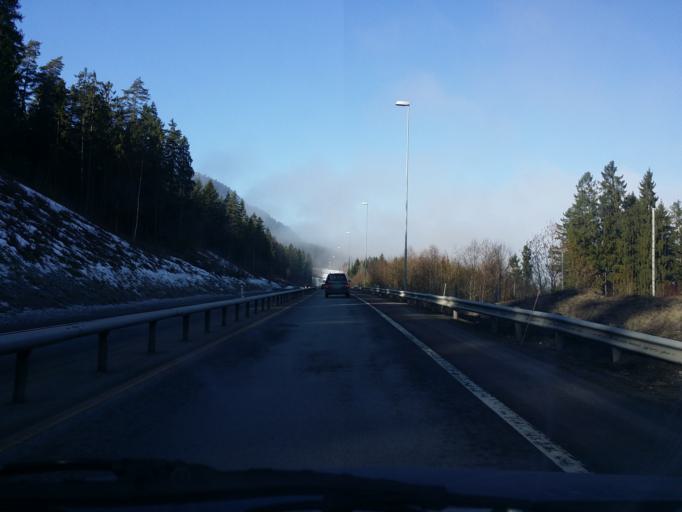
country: NO
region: Buskerud
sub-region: Nedre Eiker
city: Mjondalen
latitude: 59.7426
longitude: 10.0827
